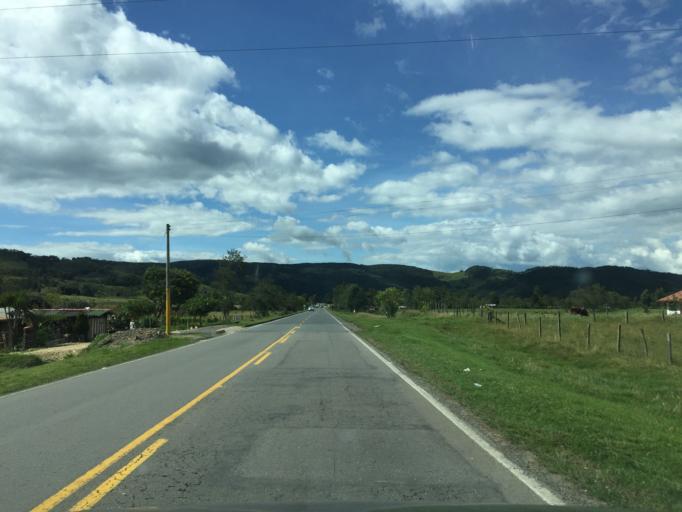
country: CO
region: Boyaca
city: Arcabuco
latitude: 5.7767
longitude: -73.4592
